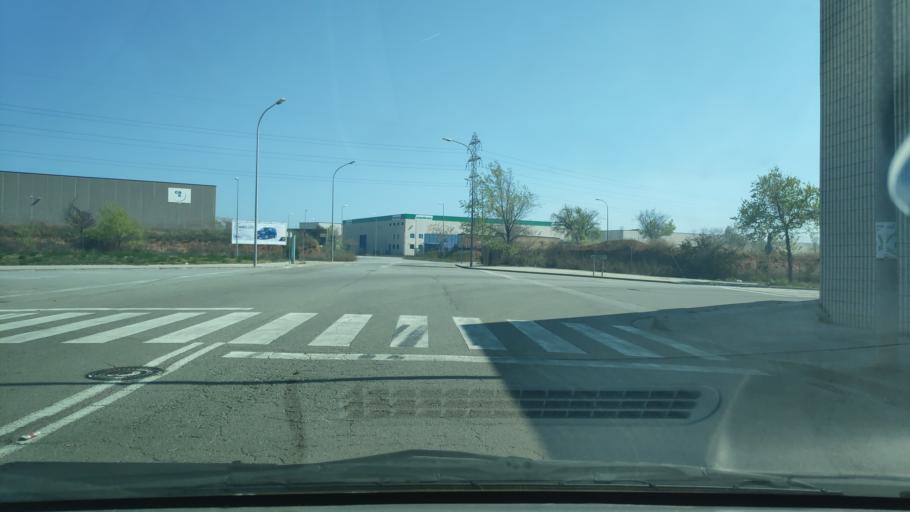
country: ES
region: Catalonia
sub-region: Provincia de Barcelona
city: Polinya
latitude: 41.5421
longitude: 2.1321
